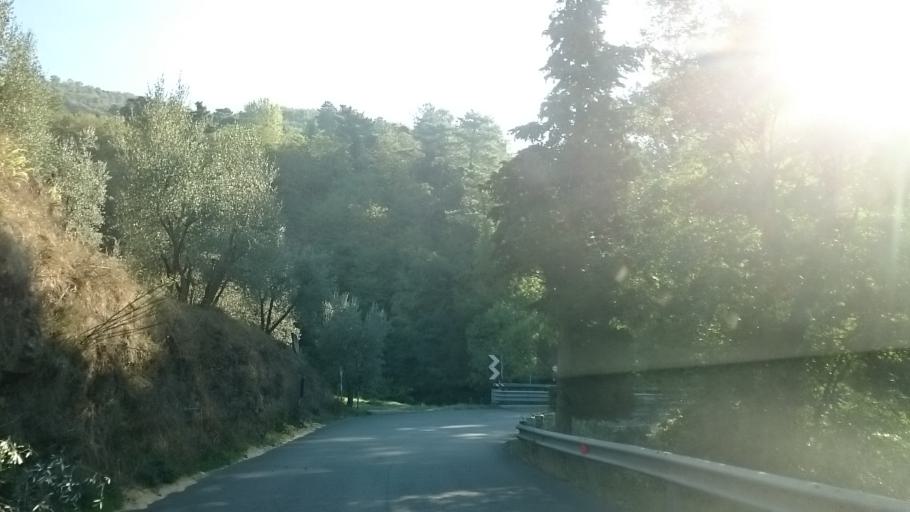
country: IT
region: Tuscany
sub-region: Province of Florence
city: Reggello
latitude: 43.6917
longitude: 11.5356
